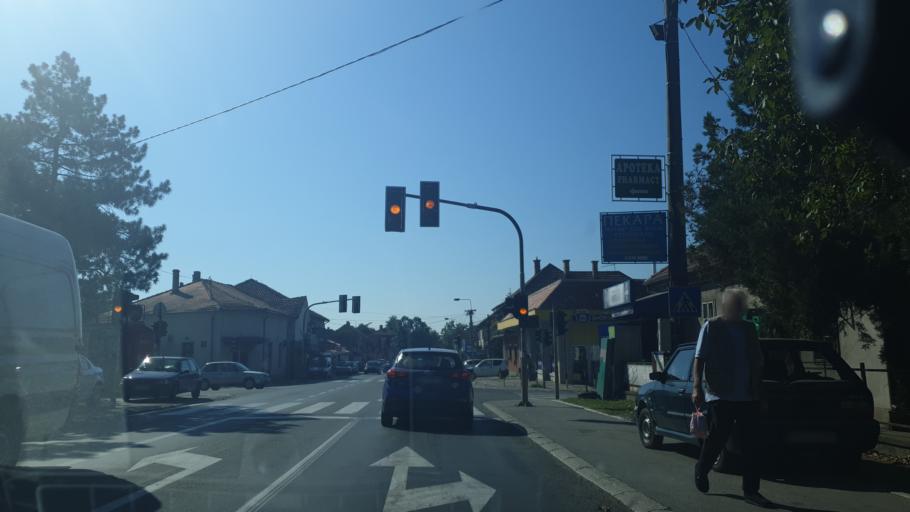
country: RS
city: Stepojevac
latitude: 44.5139
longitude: 20.2935
